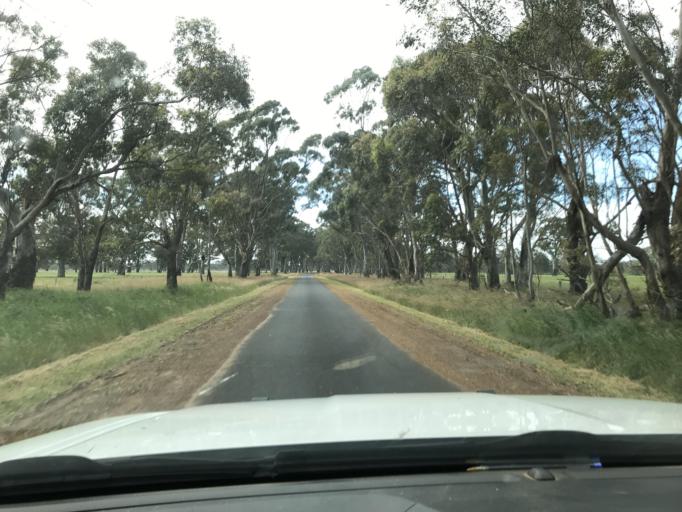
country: AU
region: South Australia
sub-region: Wattle Range
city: Penola
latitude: -37.1783
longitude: 141.2769
